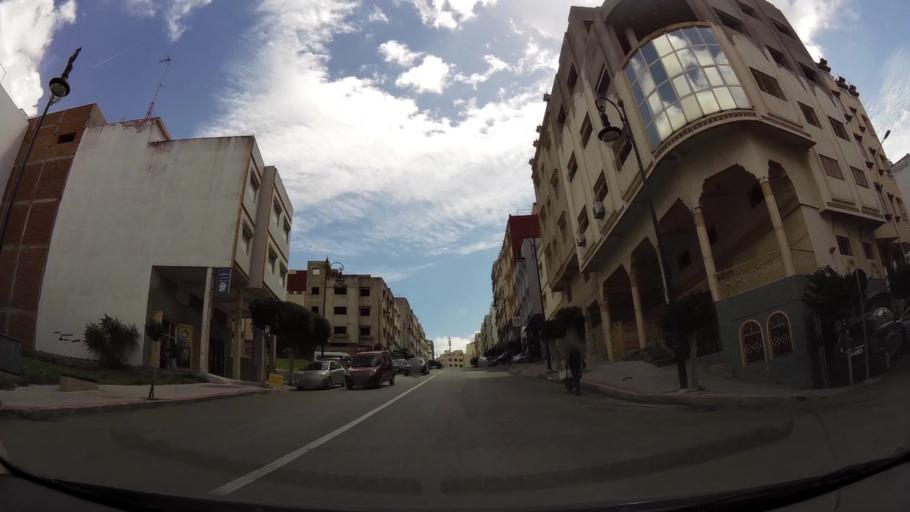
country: MA
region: Tanger-Tetouan
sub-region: Tanger-Assilah
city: Tangier
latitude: 35.7541
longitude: -5.8303
